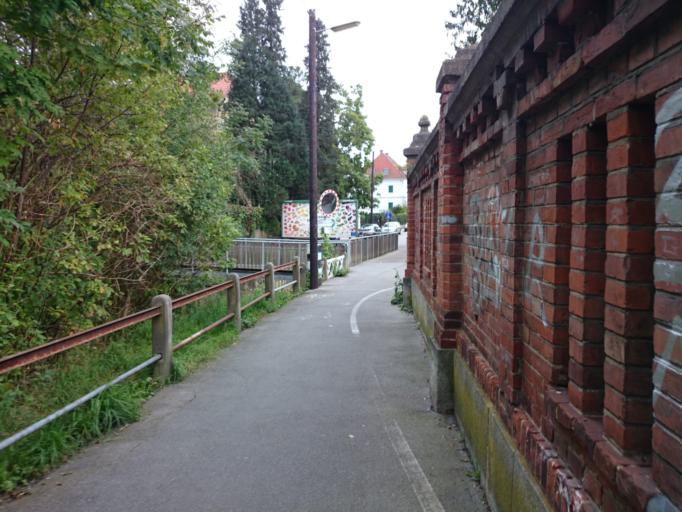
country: AT
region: Styria
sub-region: Graz Stadt
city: Graz
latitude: 47.0727
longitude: 15.4581
